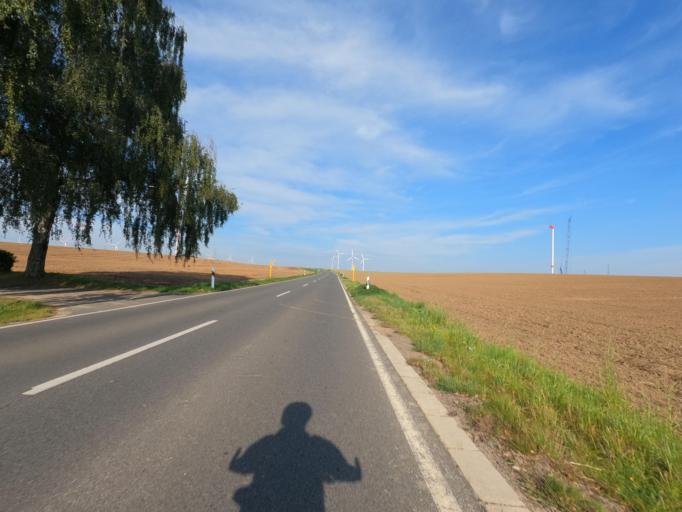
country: DE
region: North Rhine-Westphalia
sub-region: Regierungsbezirk Koln
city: Linnich
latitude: 50.9820
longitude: 6.2509
